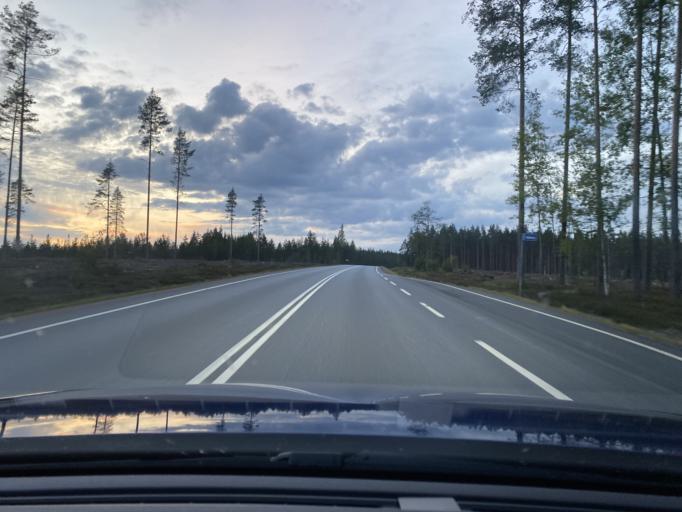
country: FI
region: Southern Ostrobothnia
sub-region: Suupohja
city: Kauhajoki
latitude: 62.2283
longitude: 22.2724
